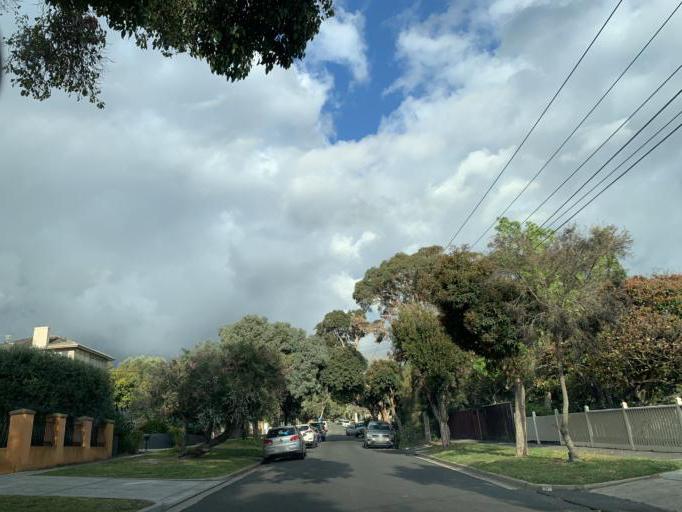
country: AU
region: Victoria
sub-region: Bayside
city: Black Rock
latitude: -37.9787
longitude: 145.0255
